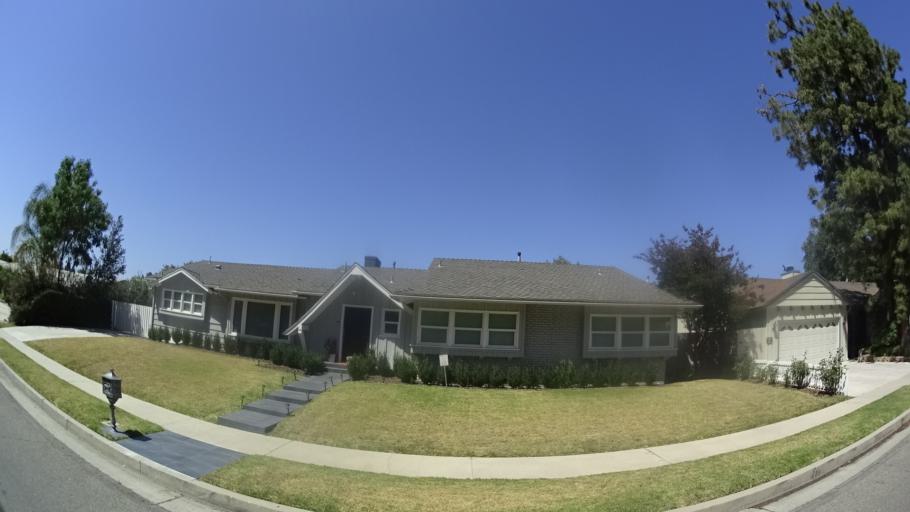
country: US
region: California
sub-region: Los Angeles County
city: Sherman Oaks
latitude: 34.1451
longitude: -118.4914
